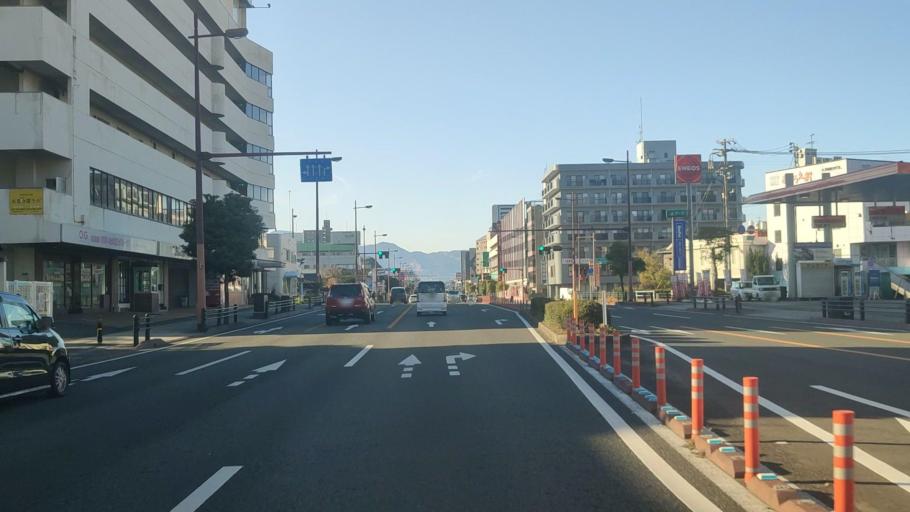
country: JP
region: Oita
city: Oita
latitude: 33.2431
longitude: 131.5892
